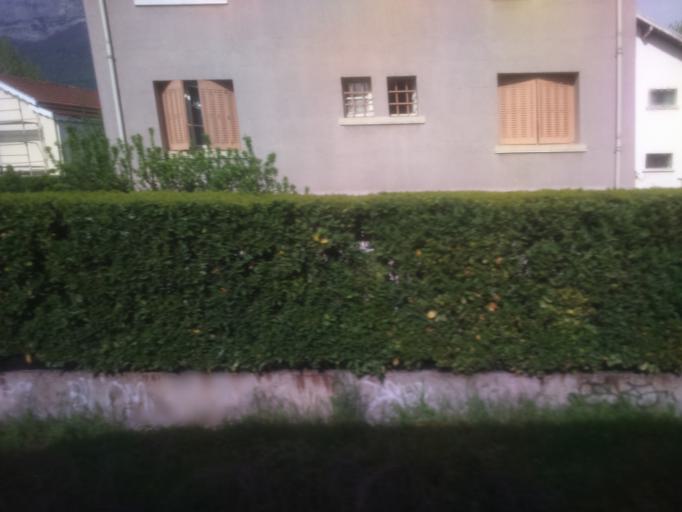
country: FR
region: Rhone-Alpes
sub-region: Departement de l'Isere
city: Grenoble
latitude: 45.1543
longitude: 5.7084
